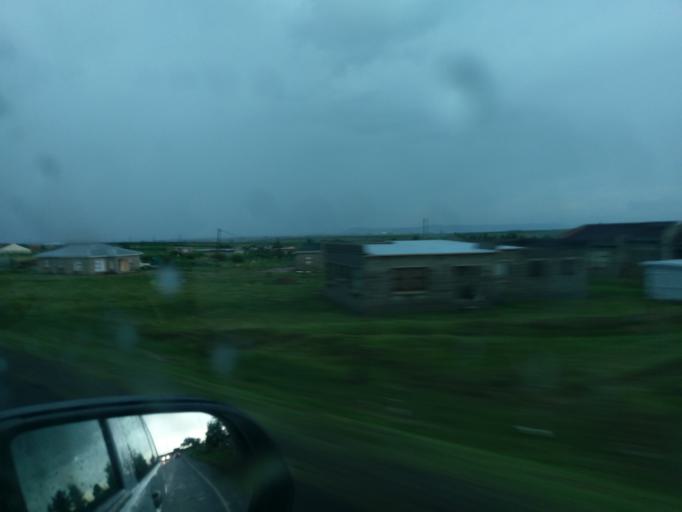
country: LS
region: Maseru
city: Maseru
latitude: -29.4811
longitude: 27.5223
